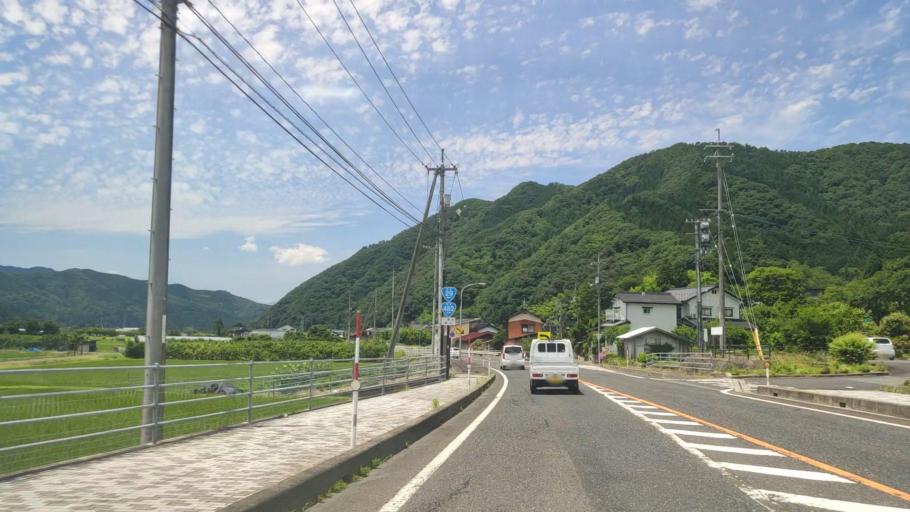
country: JP
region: Tottori
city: Tottori
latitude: 35.3662
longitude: 134.3394
